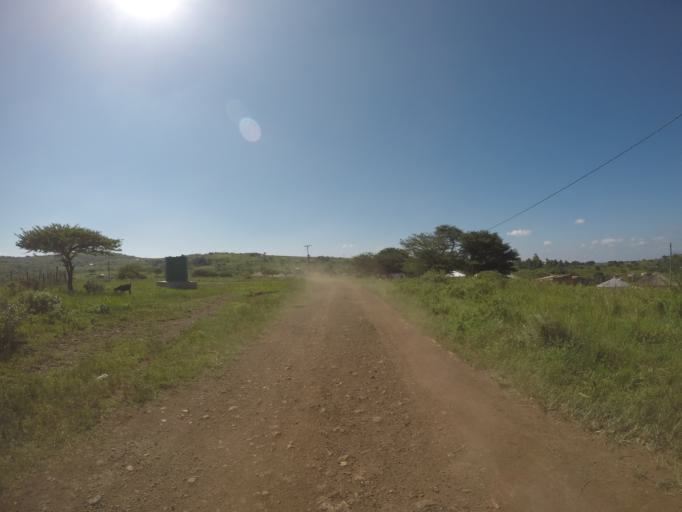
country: ZA
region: KwaZulu-Natal
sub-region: uThungulu District Municipality
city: Empangeni
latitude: -28.5686
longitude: 31.7001
